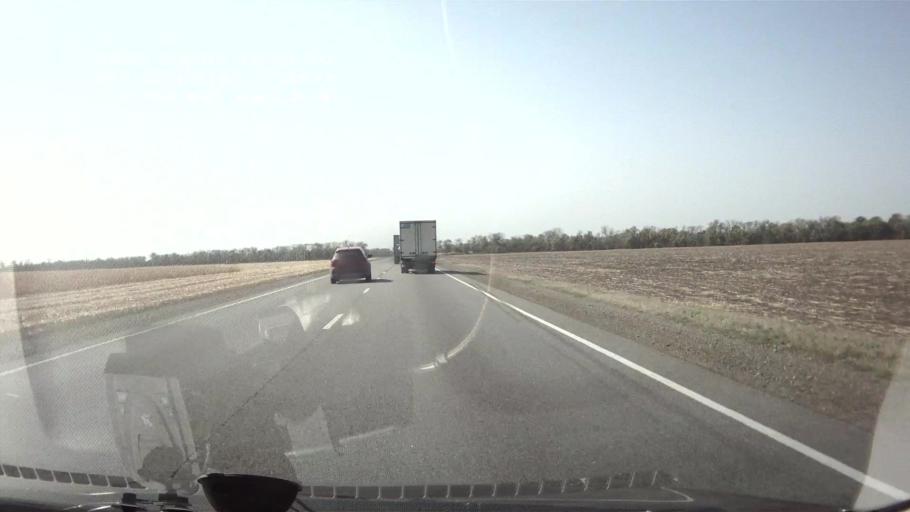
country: RU
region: Krasnodarskiy
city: Kazanskaya
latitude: 45.4299
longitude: 40.3187
